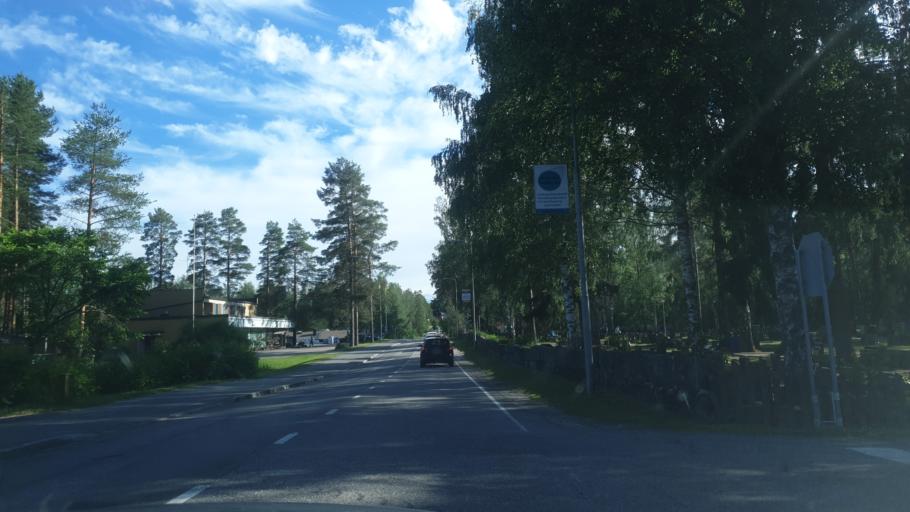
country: FI
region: Southern Savonia
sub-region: Mikkeli
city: Pertunmaa
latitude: 61.5072
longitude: 26.4821
